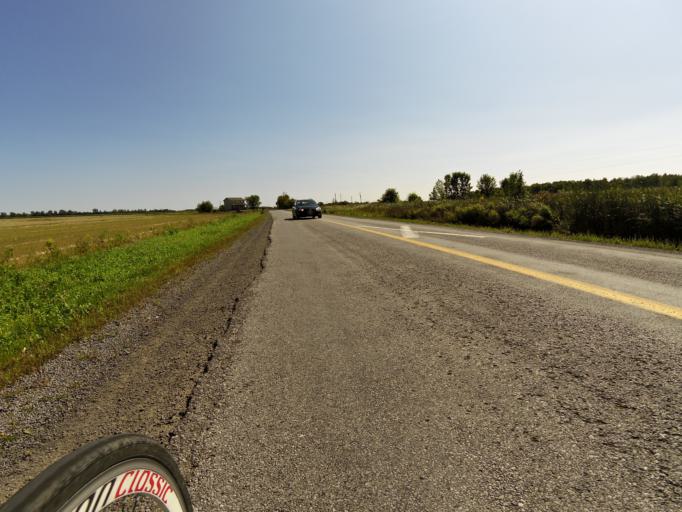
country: CA
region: Ontario
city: Arnprior
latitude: 45.4494
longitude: -76.0827
